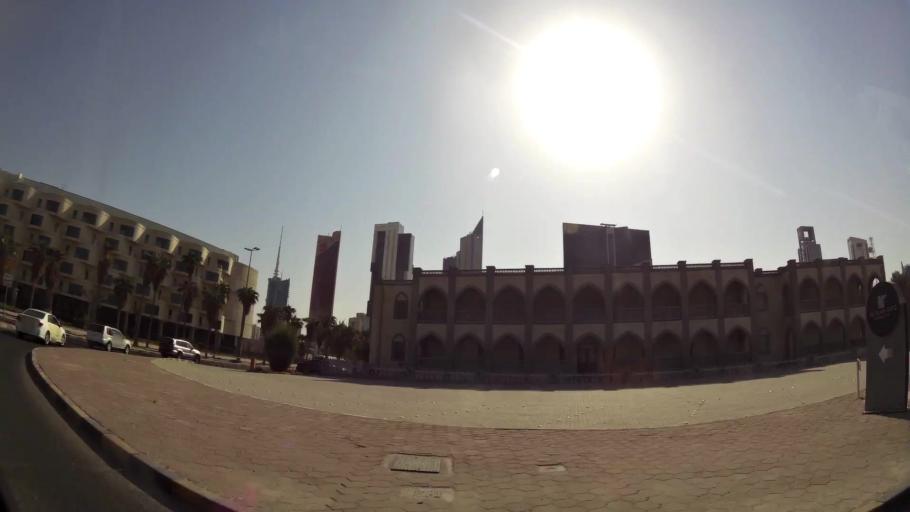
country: KW
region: Al Asimah
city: Kuwait City
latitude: 29.3684
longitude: 47.9619
